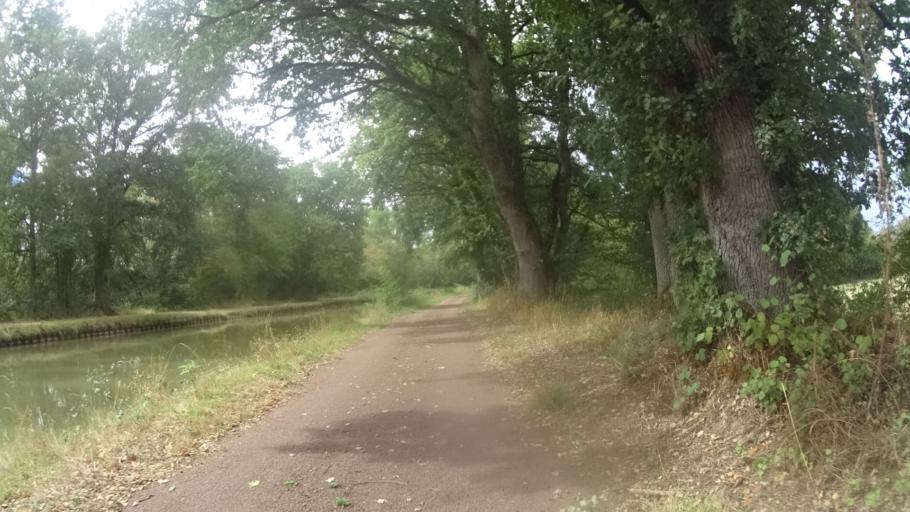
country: FR
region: Bourgogne
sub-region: Departement de la Nievre
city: Imphy
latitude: 46.9130
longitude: 3.2452
